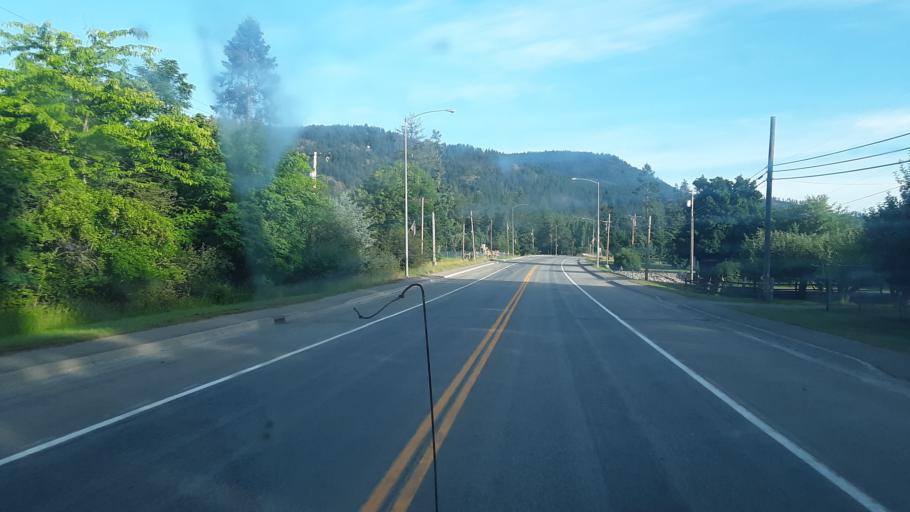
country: US
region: Montana
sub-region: Lincoln County
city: Libby
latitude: 48.4503
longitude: -115.8815
